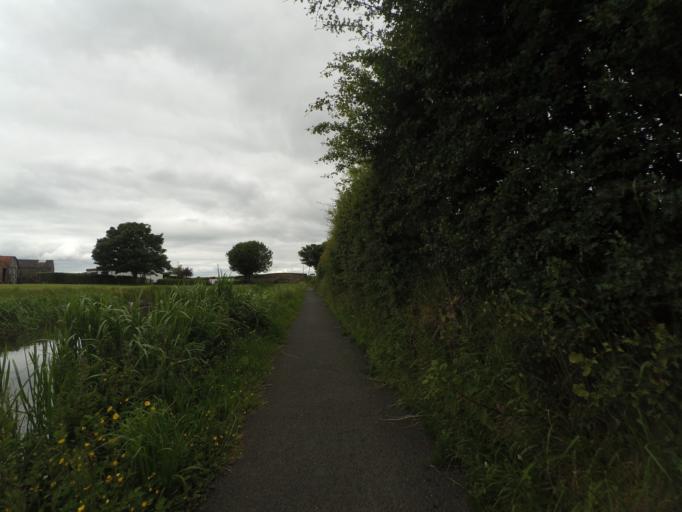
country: GB
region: Scotland
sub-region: West Lothian
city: Linlithgow
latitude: 55.9760
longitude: -3.5374
